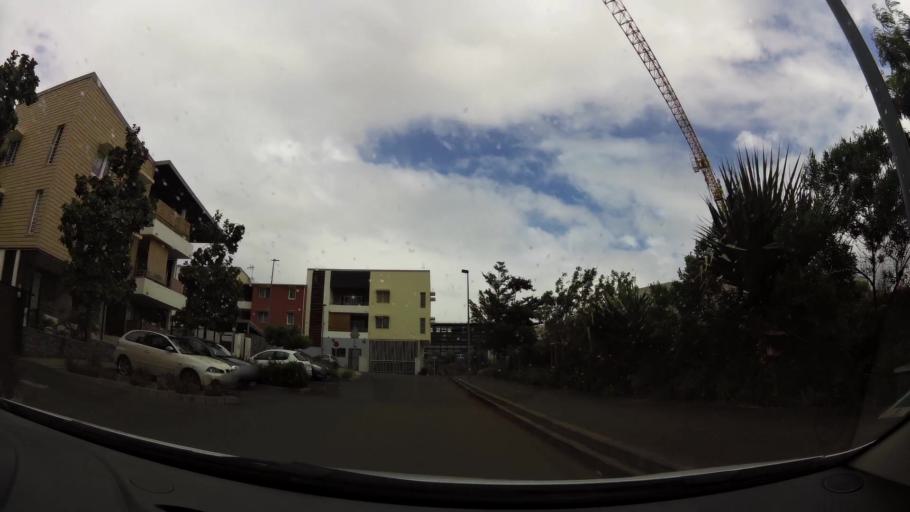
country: RE
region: Reunion
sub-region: Reunion
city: Sainte-Suzanne
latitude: -20.9017
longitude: 55.5974
